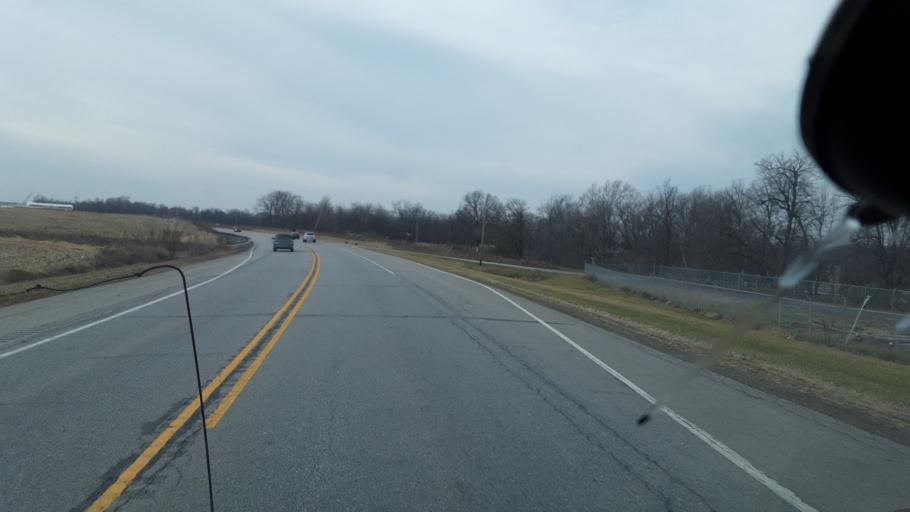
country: US
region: Indiana
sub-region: DeKalb County
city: Waterloo
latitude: 41.4390
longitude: -85.0380
